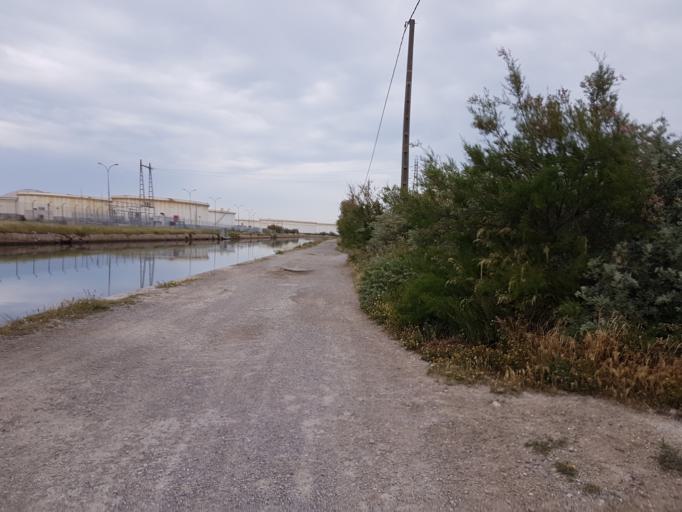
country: FR
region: Languedoc-Roussillon
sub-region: Departement de l'Herault
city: Frontignan
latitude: 43.4377
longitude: 3.7524
